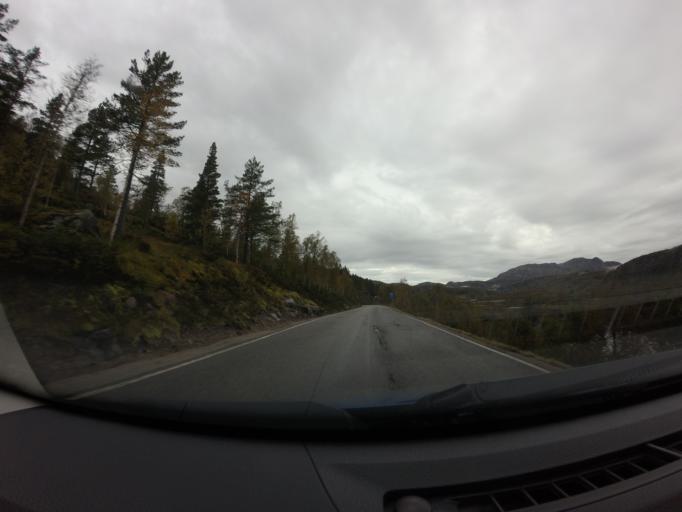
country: NO
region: Vest-Agder
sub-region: Sirdal
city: Tonstad
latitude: 58.9348
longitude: 6.9121
